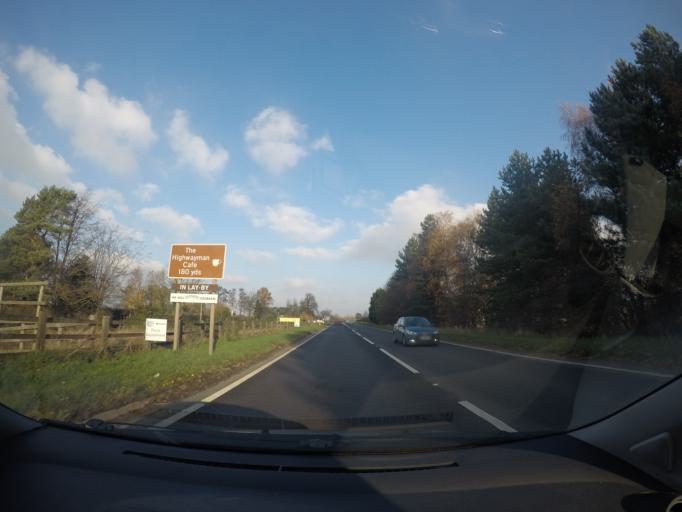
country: GB
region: England
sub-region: City of York
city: Murton
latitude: 54.0006
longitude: -1.0146
